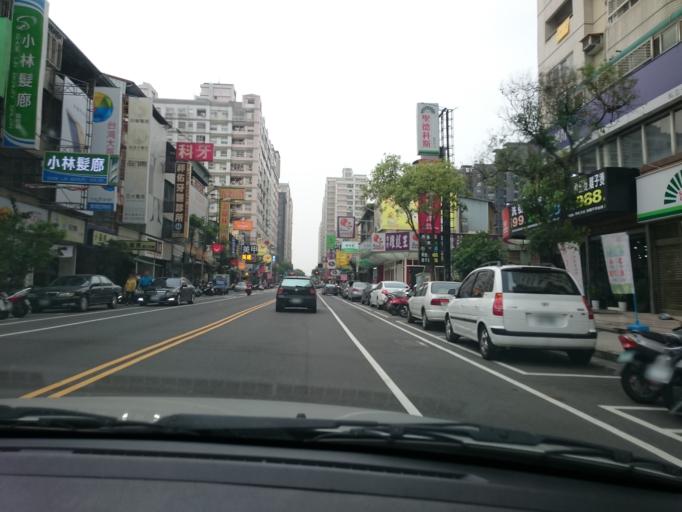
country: TW
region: Taiwan
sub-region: Taichung City
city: Taichung
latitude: 24.1494
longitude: 120.6356
